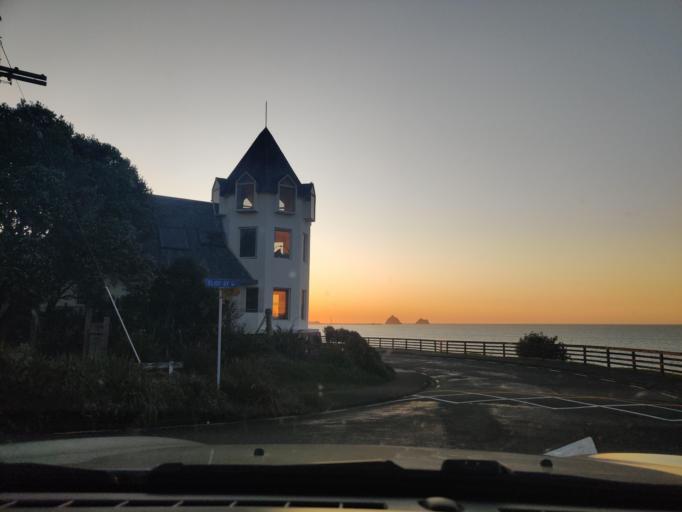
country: NZ
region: Taranaki
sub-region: New Plymouth District
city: New Plymouth
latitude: -39.0519
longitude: 174.0812
